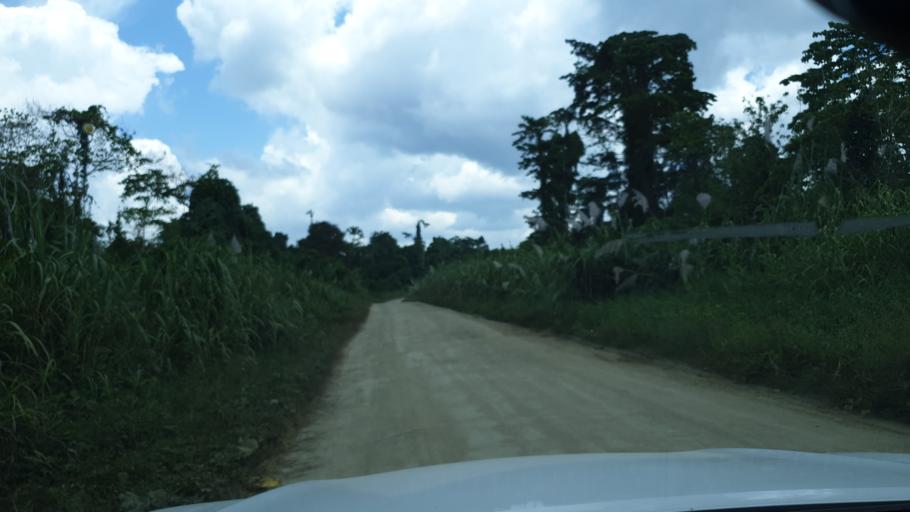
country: PG
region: East Sepik
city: Angoram
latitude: -3.8977
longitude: 143.9255
